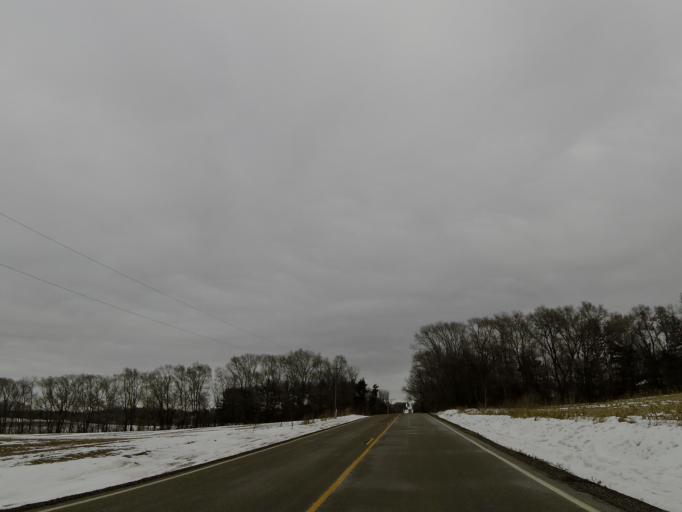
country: US
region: Wisconsin
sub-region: Pierce County
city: Prescott
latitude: 44.8189
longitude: -92.8304
